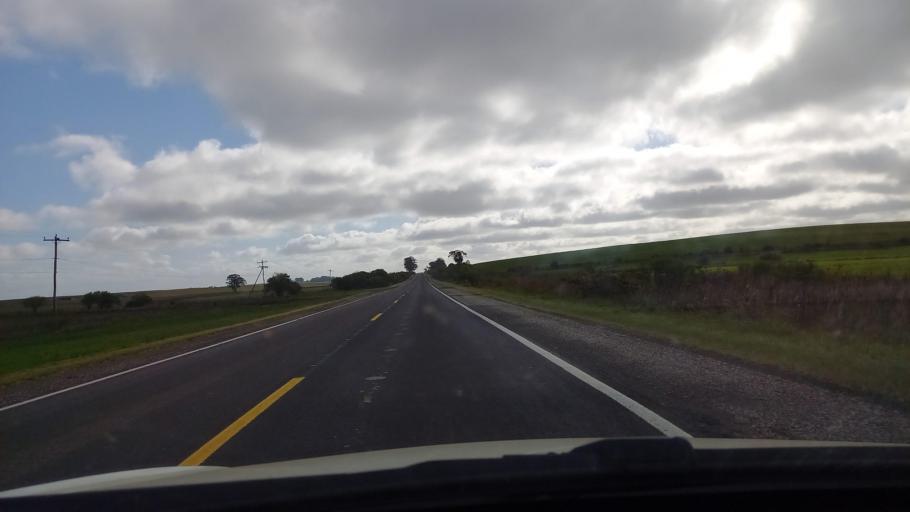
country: BR
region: Rio Grande do Sul
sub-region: Dom Pedrito
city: Dom Pedrito
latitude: -30.8963
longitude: -54.8467
